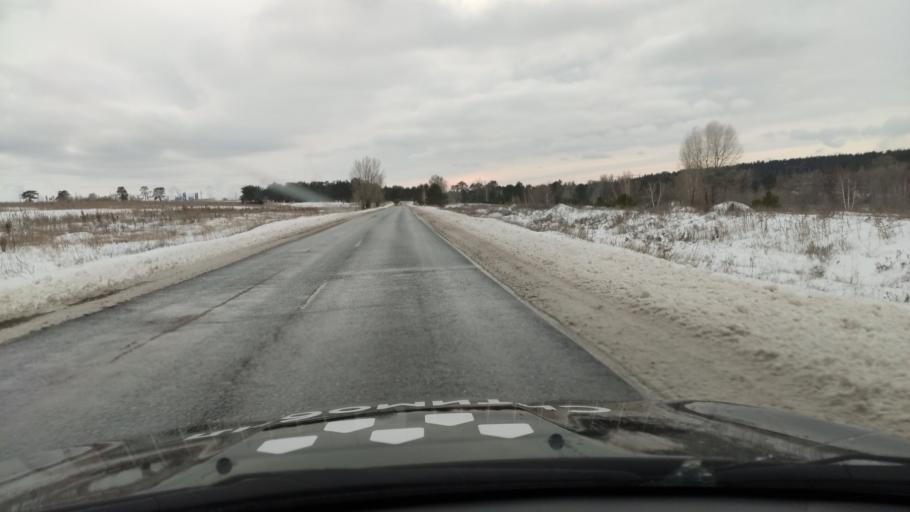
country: RU
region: Samara
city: Povolzhskiy
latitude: 53.5616
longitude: 49.6480
